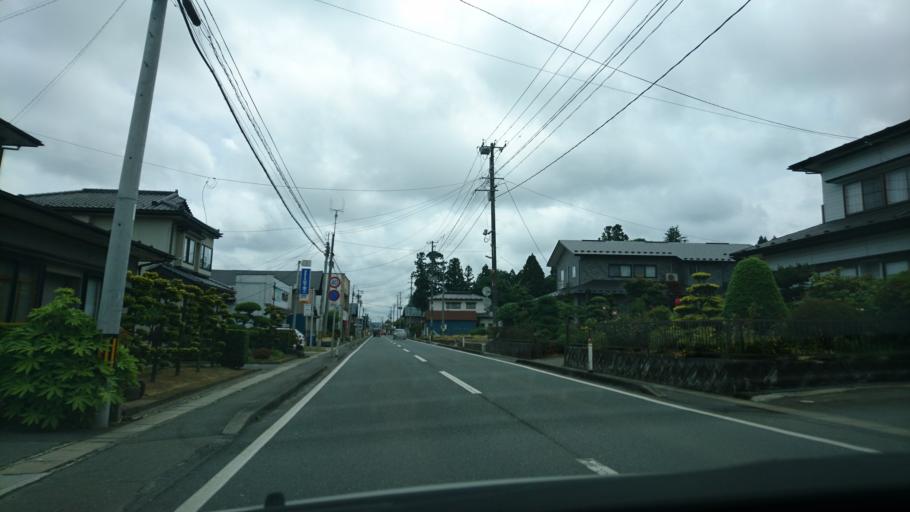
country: JP
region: Iwate
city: Ichinoseki
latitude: 38.9555
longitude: 141.1297
